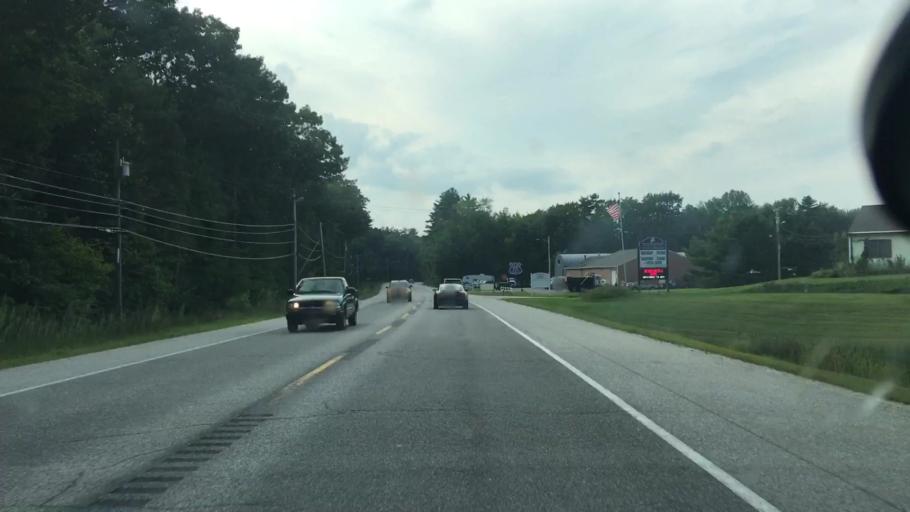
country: US
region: Maine
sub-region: Cumberland County
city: North Windham
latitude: 43.8598
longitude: -70.4591
